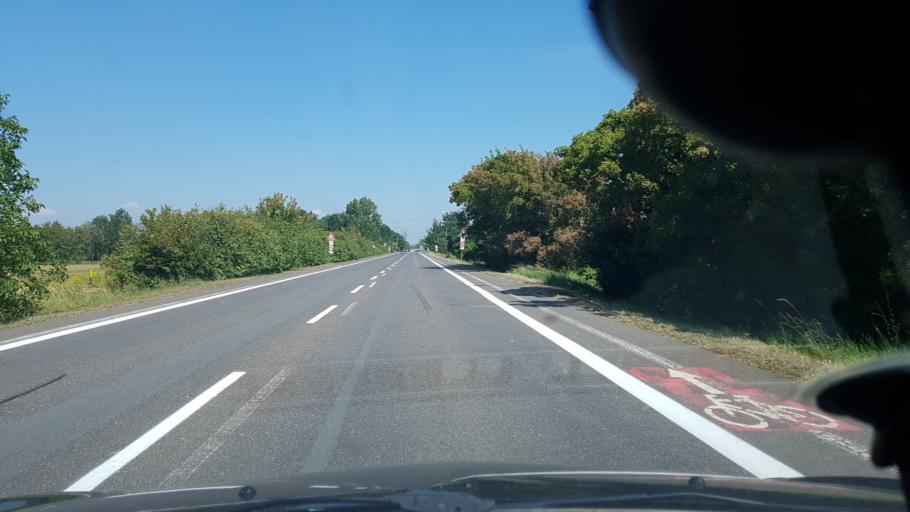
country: CZ
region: Moravskoslezsky
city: Stary Bohumin
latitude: 49.9032
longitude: 18.3357
